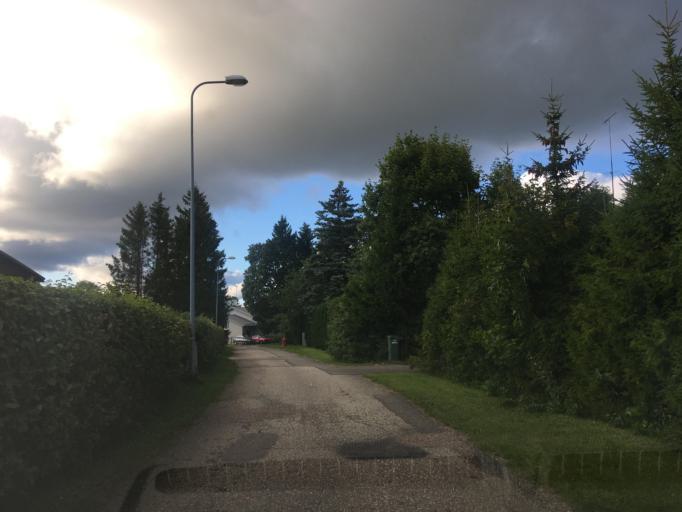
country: EE
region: Raplamaa
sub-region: Maerjamaa vald
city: Marjamaa
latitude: 58.9040
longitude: 24.4377
